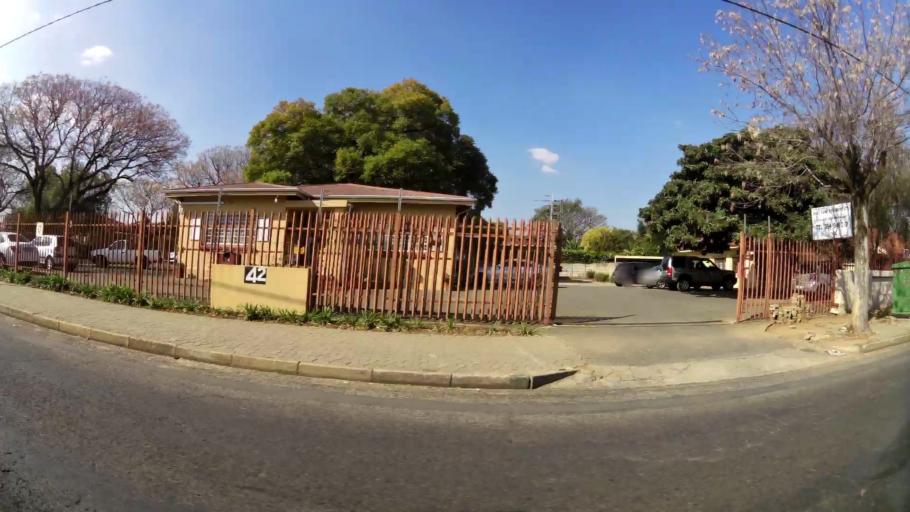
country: ZA
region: Gauteng
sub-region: City of Johannesburg Metropolitan Municipality
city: Modderfontein
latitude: -26.0963
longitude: 28.2345
